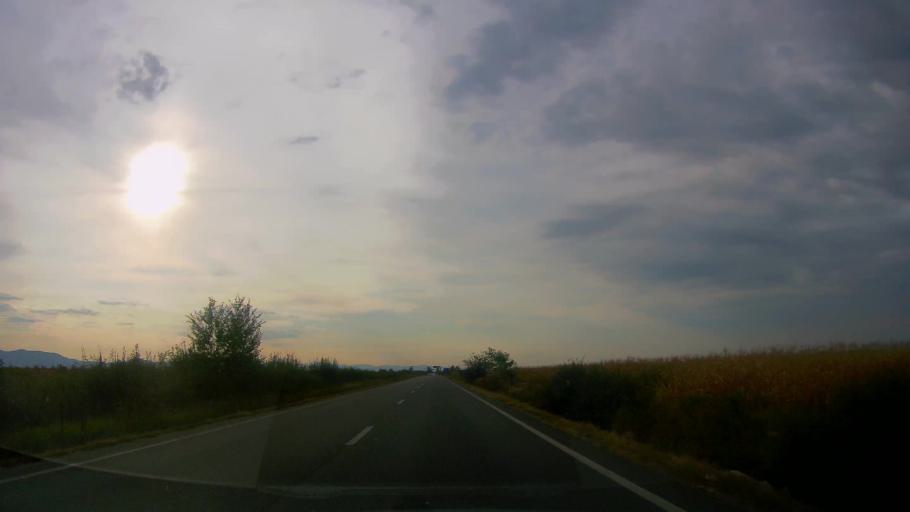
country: RO
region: Satu Mare
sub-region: Comuna Halmeu
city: Halmeu
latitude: 47.9608
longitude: 23.0497
